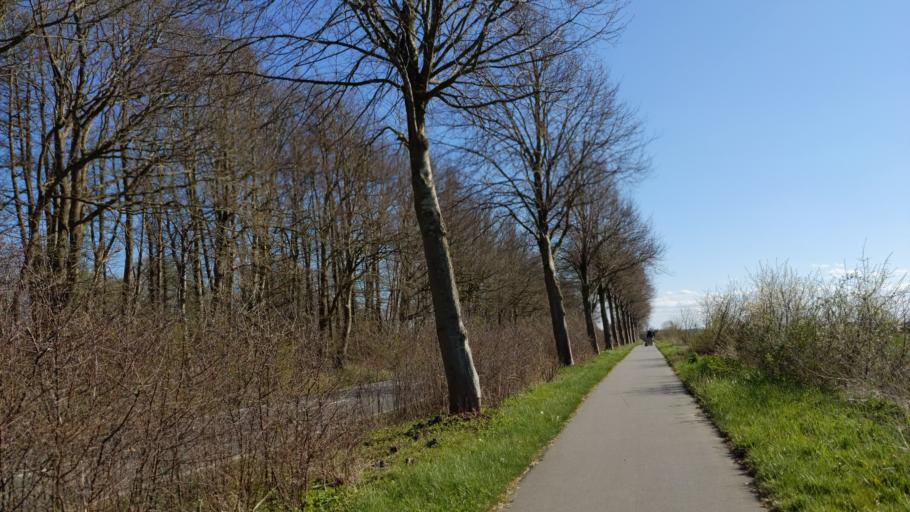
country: DE
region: Schleswig-Holstein
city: Eutin
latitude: 54.1129
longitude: 10.6110
